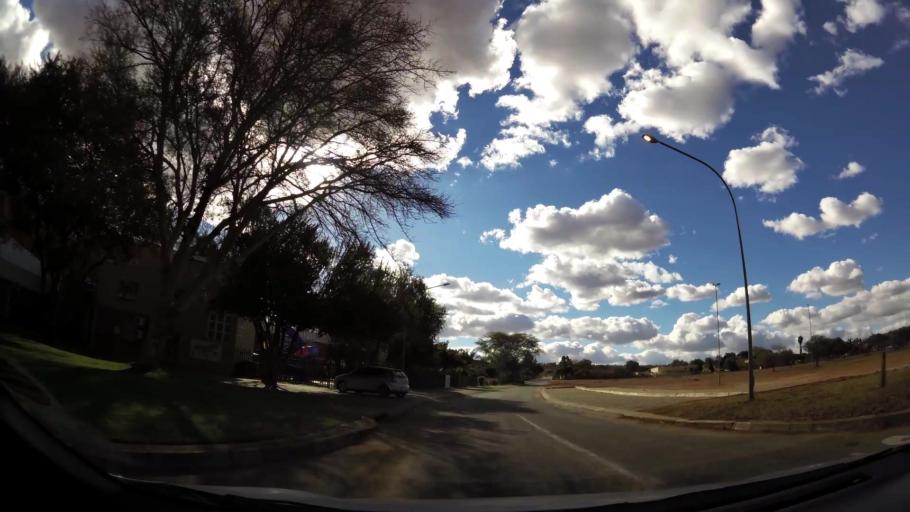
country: ZA
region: Limpopo
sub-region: Capricorn District Municipality
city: Polokwane
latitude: -23.9047
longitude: 29.4956
